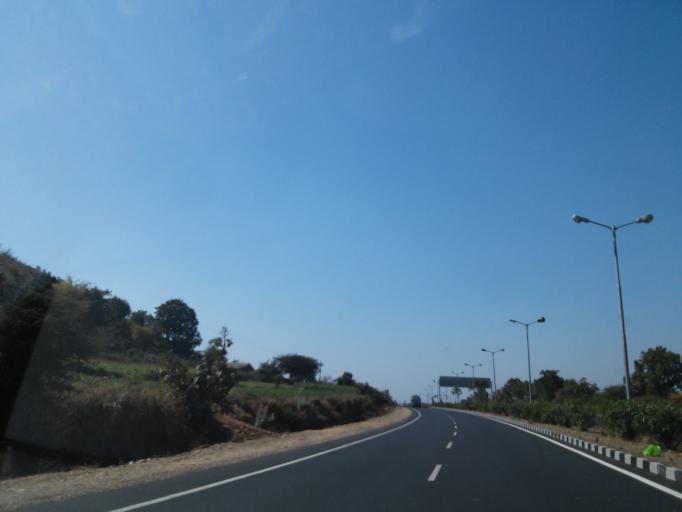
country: IN
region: Gujarat
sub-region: Sabar Kantha
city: Modasa
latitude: 23.6140
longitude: 73.2466
